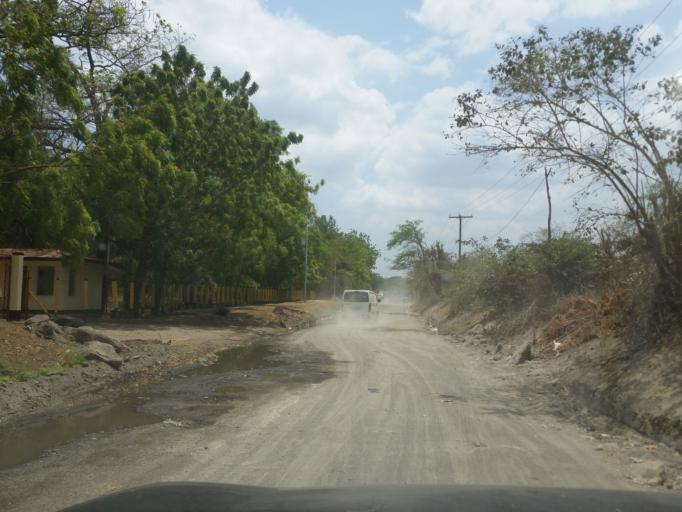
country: NI
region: Managua
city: Managua
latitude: 12.1251
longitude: -86.1652
